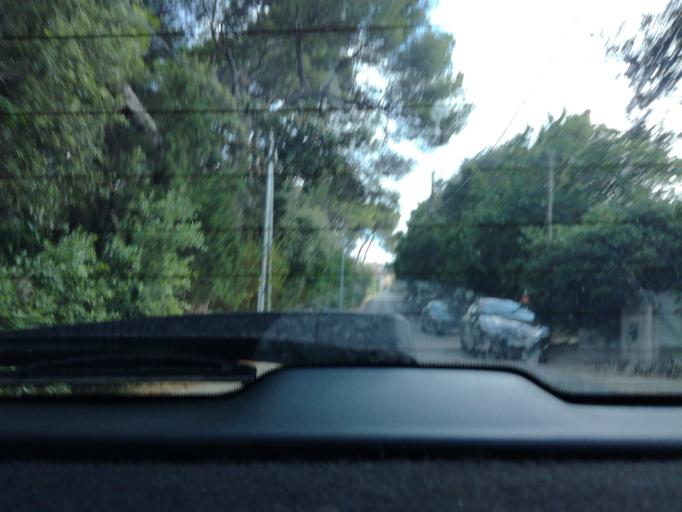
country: FR
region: Provence-Alpes-Cote d'Azur
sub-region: Departement du Var
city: Hyeres
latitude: 43.0414
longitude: 6.1328
